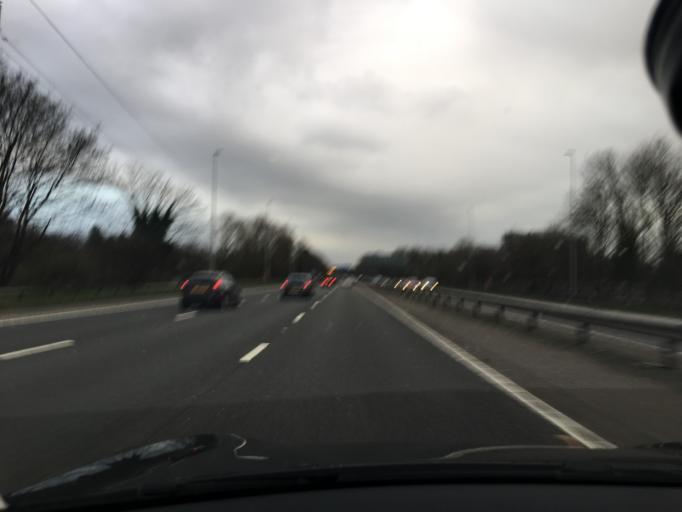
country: GB
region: England
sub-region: Manchester
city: Didsbury
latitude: 53.4074
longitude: -2.2496
